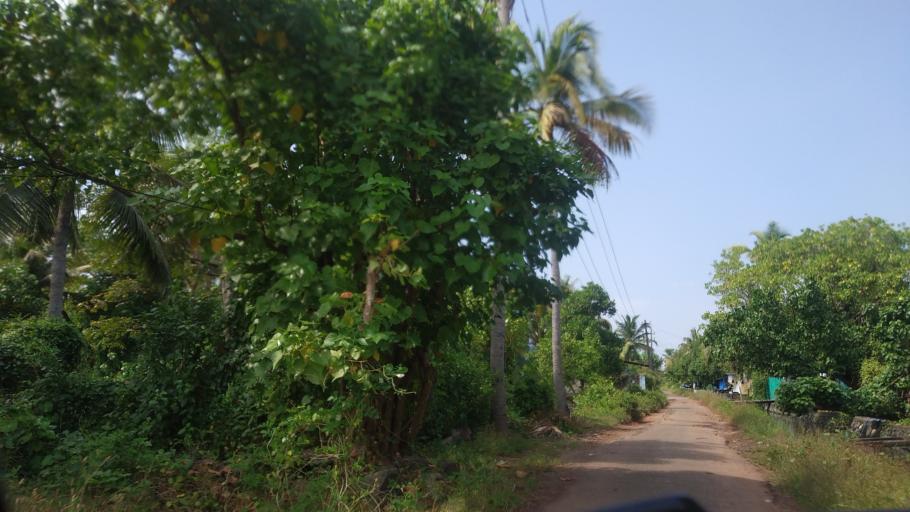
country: IN
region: Kerala
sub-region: Ernakulam
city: Elur
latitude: 10.0800
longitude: 76.2040
